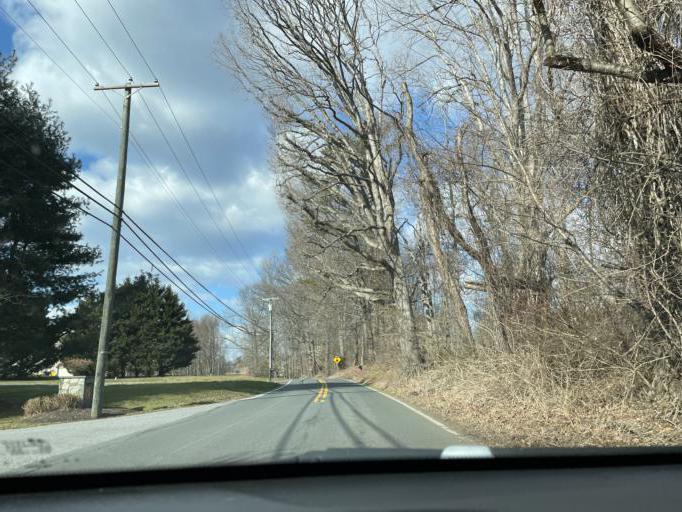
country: US
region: Maryland
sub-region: Anne Arundel County
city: Gambrills
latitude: 39.0362
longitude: -76.6542
